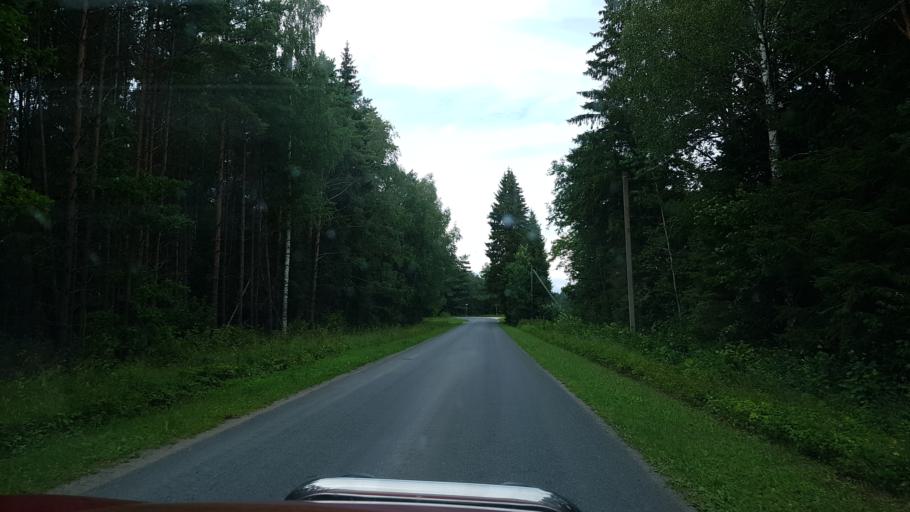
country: EE
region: Laeaene
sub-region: Ridala Parish
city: Uuemoisa
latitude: 59.0057
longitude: 23.7235
